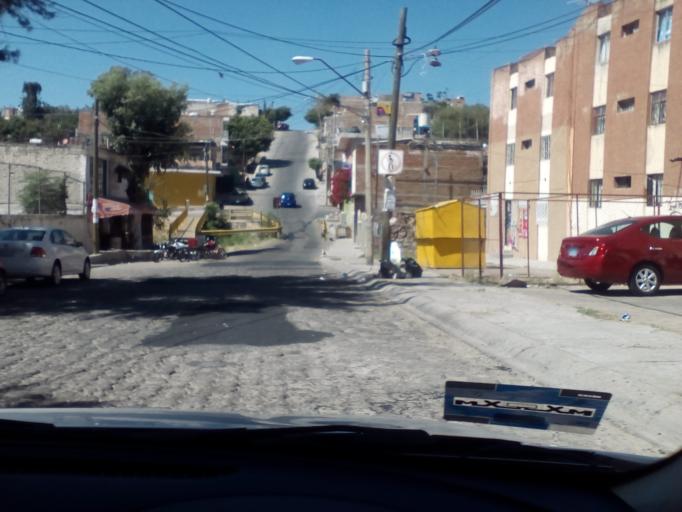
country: MX
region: Guanajuato
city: Leon
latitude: 21.1220
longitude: -101.7075
